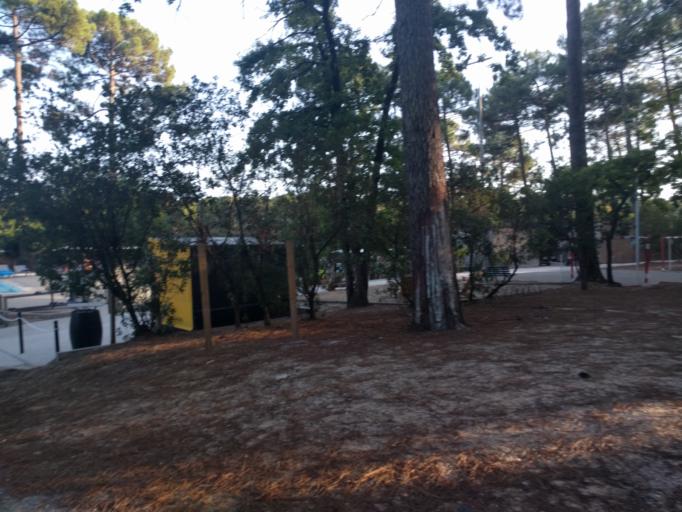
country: FR
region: Aquitaine
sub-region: Departement de la Gironde
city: Ares
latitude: 44.7529
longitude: -1.1873
